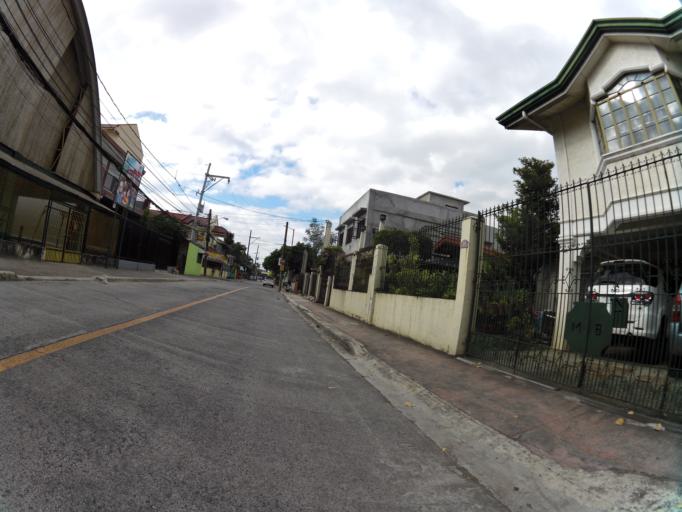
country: PH
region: Calabarzon
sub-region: Province of Rizal
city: Antipolo
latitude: 14.6429
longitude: 121.1097
